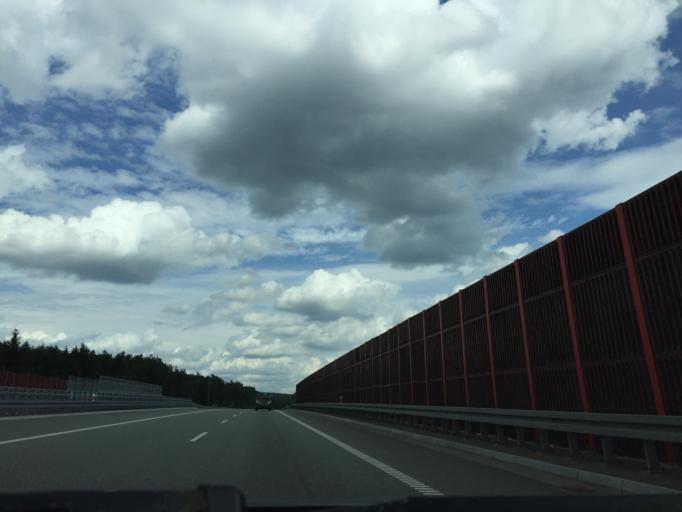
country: PL
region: Swietokrzyskie
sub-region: Powiat kielecki
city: Kostomloty Pierwsze
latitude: 50.9205
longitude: 20.6160
